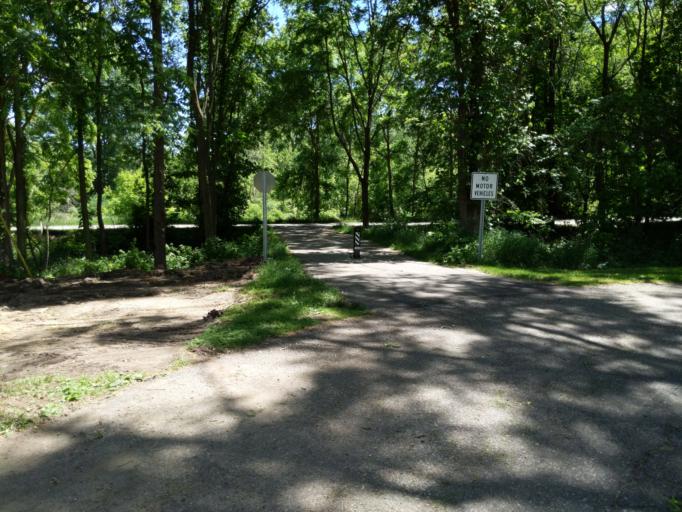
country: US
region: Michigan
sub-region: Ingham County
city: Stockbridge
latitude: 42.4506
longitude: -84.1731
